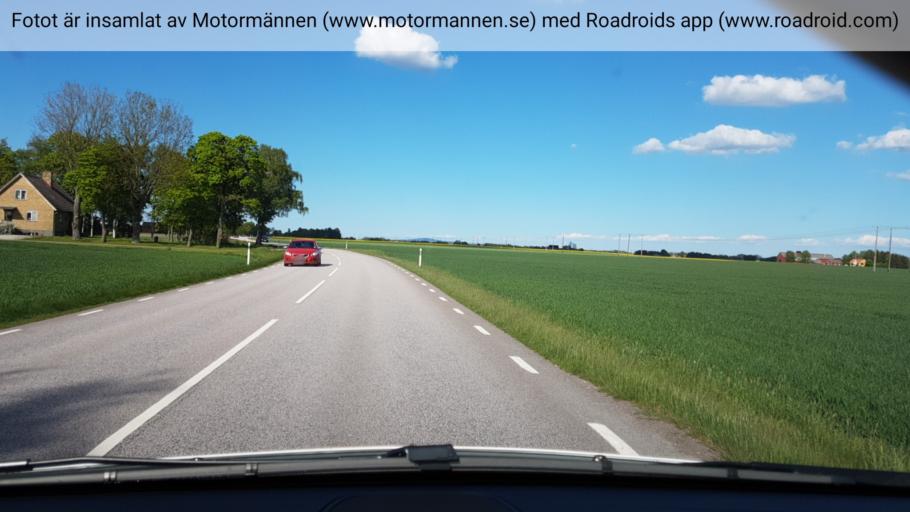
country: SE
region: Vaestra Goetaland
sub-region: Lidkopings Kommun
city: Lidkoping
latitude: 58.4396
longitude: 13.0633
